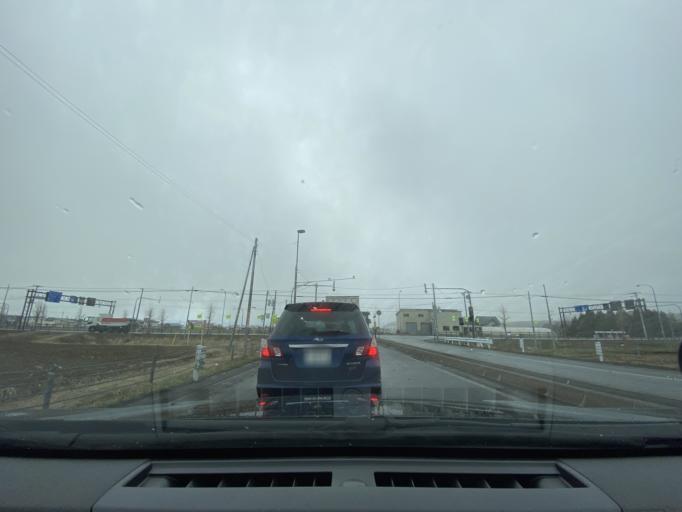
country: JP
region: Hokkaido
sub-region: Asahikawa-shi
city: Asahikawa
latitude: 43.8344
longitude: 142.4059
